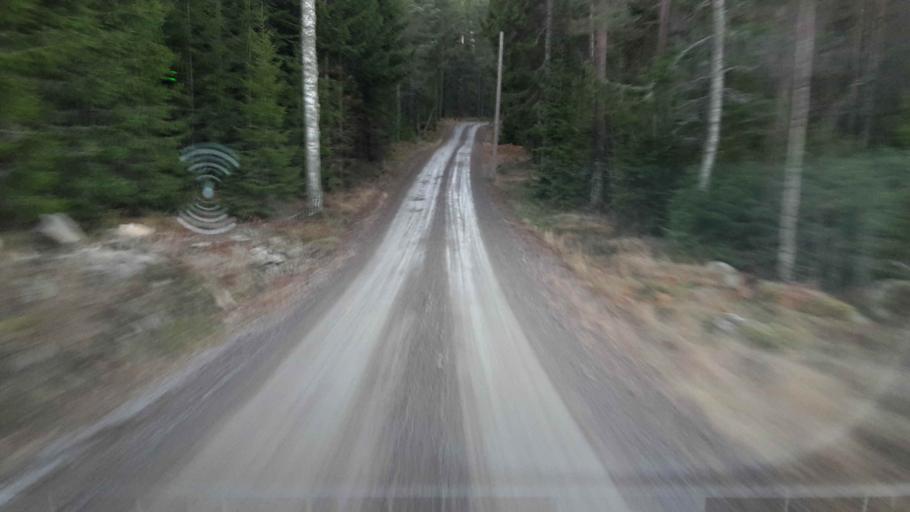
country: SE
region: OEstergoetland
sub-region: Atvidabergs Kommun
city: Atvidaberg
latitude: 58.2590
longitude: 16.0667
